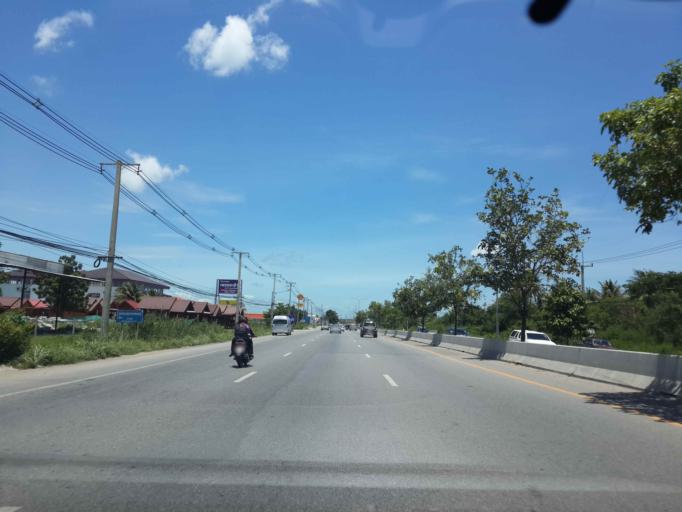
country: TH
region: Phetchaburi
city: Cha-am
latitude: 12.8606
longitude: 99.9214
